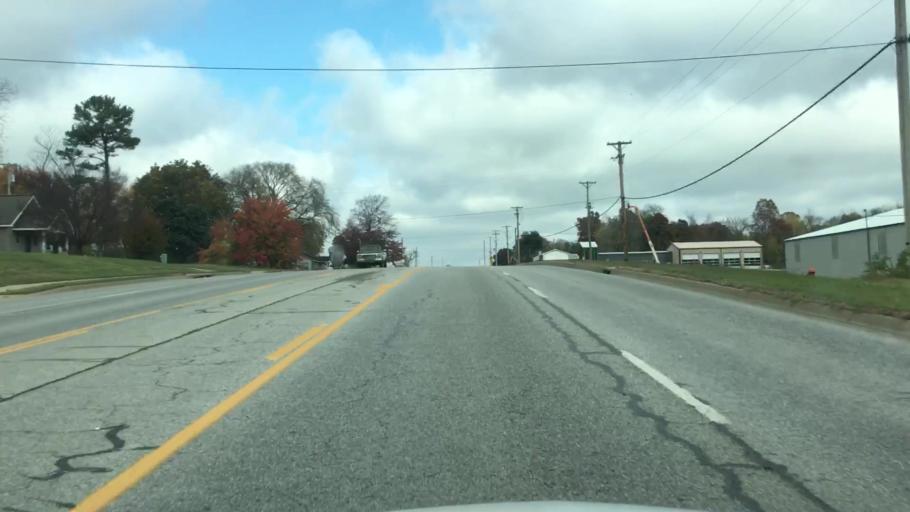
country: US
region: Arkansas
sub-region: Benton County
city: Gentry
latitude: 36.2546
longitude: -94.4852
